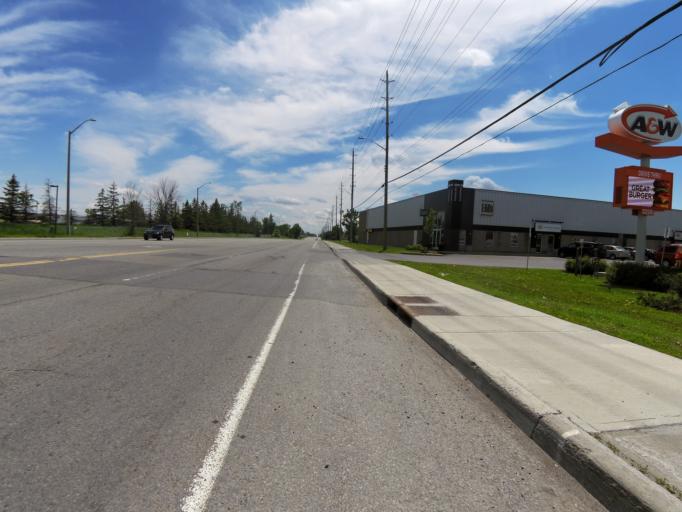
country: CA
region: Ontario
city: Ottawa
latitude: 45.3817
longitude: -75.6017
